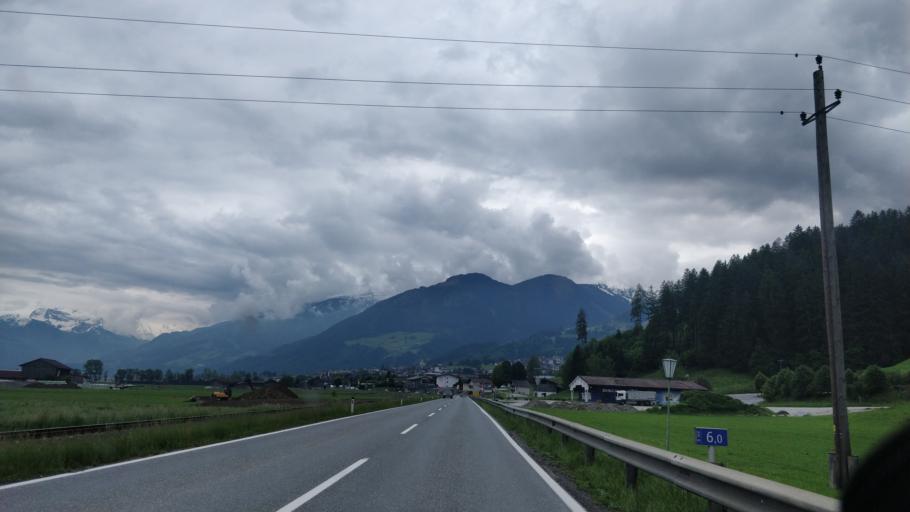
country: AT
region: Tyrol
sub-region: Politischer Bezirk Schwaz
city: Fugen
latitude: 47.3570
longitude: 11.8524
